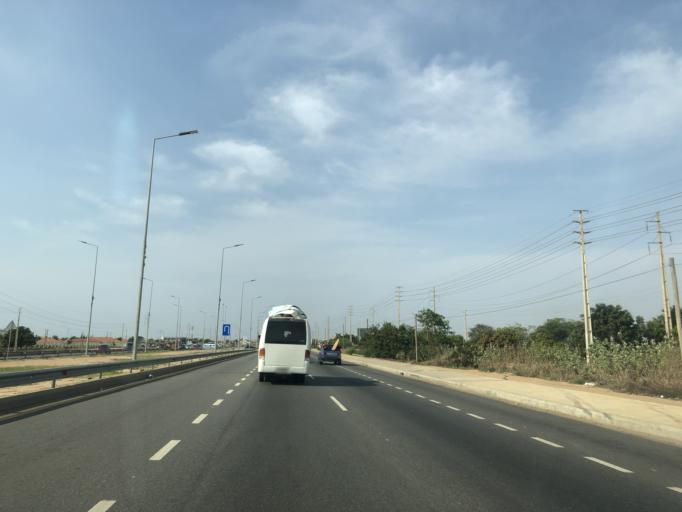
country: AO
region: Luanda
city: Luanda
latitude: -8.9487
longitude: 13.2597
